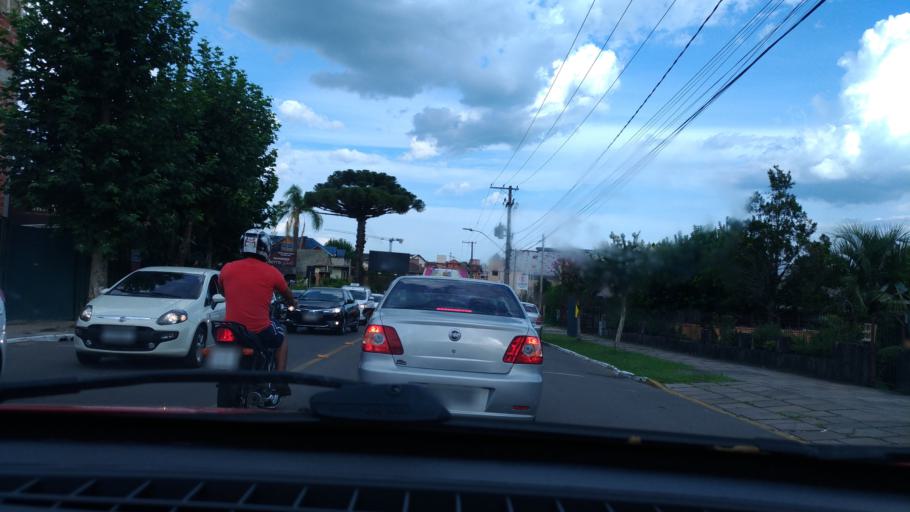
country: BR
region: Rio Grande do Sul
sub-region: Canela
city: Canela
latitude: -29.3635
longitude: -50.8177
